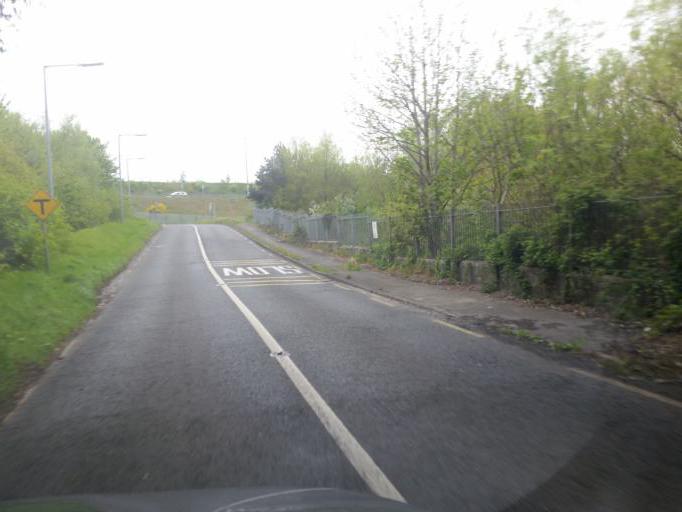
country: IE
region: Leinster
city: Castleknock
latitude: 53.3835
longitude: -6.3572
